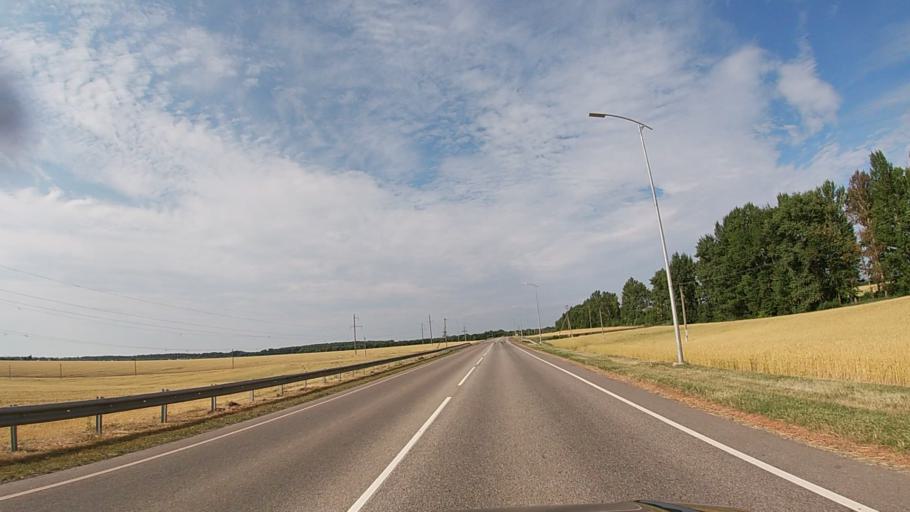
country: RU
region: Belgorod
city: Proletarskiy
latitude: 50.8097
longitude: 35.7464
